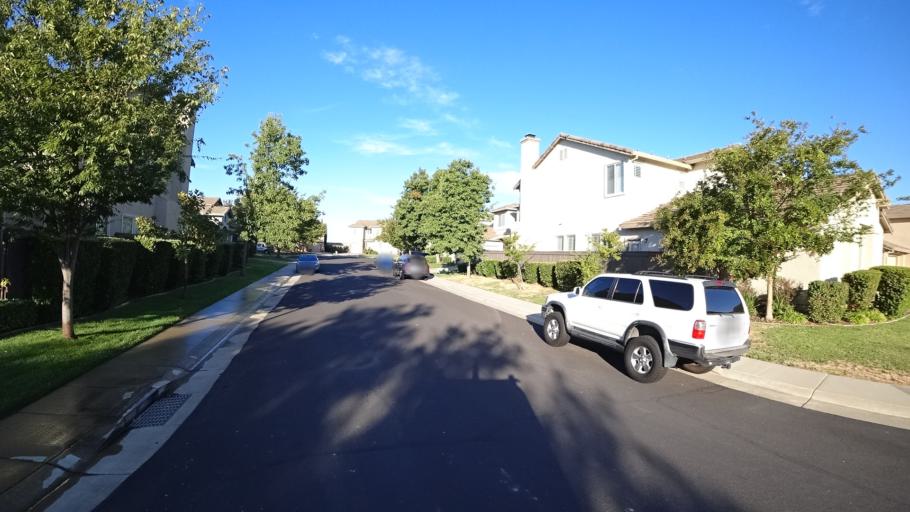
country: US
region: California
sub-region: Sacramento County
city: Laguna
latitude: 38.3990
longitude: -121.4798
